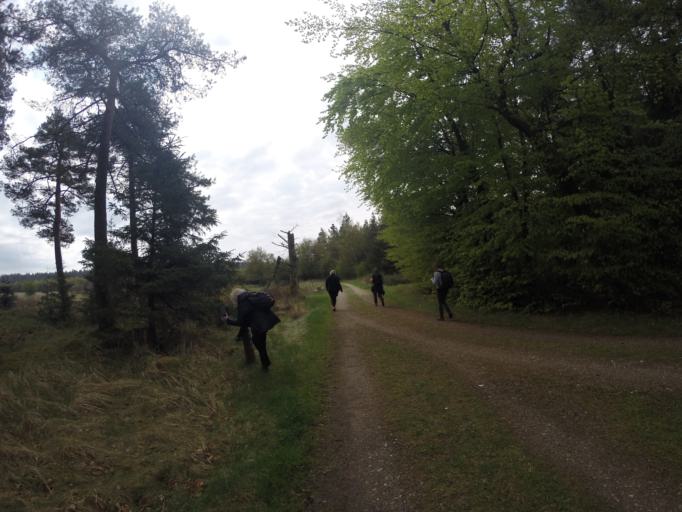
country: DK
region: North Denmark
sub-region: Thisted Kommune
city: Hanstholm
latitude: 57.0359
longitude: 8.5698
